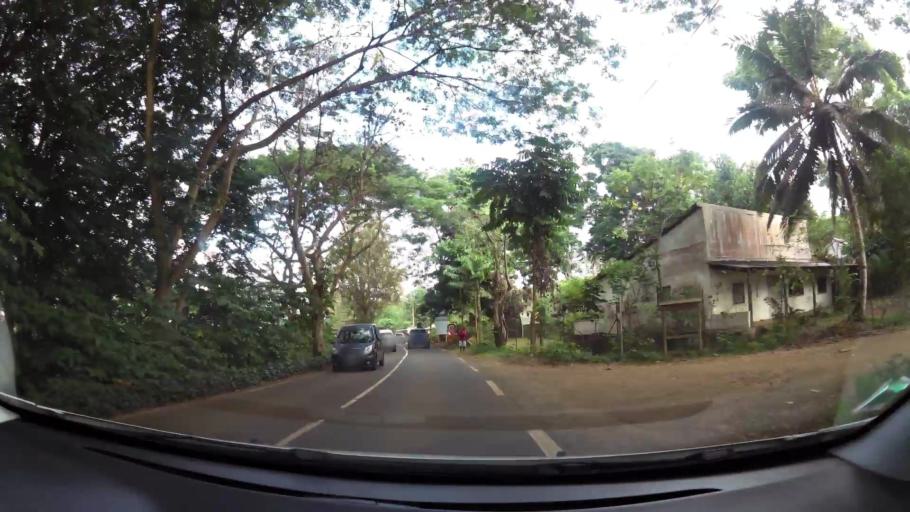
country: YT
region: Ouangani
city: Ouangani
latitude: -12.8337
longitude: 45.1339
